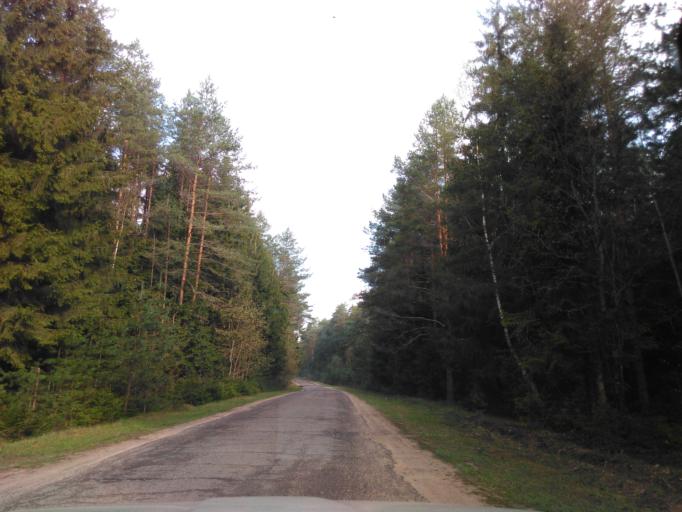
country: BY
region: Minsk
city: Rakaw
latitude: 53.9672
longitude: 27.0172
